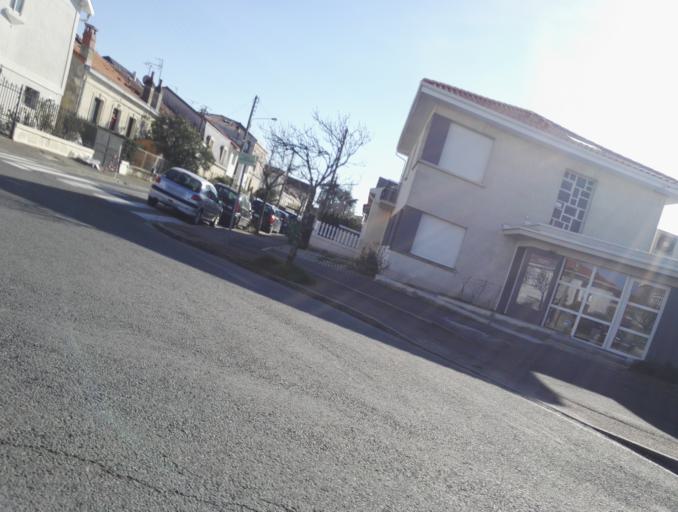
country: FR
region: Aquitaine
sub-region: Departement de la Gironde
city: Merignac
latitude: 44.8322
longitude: -0.6159
